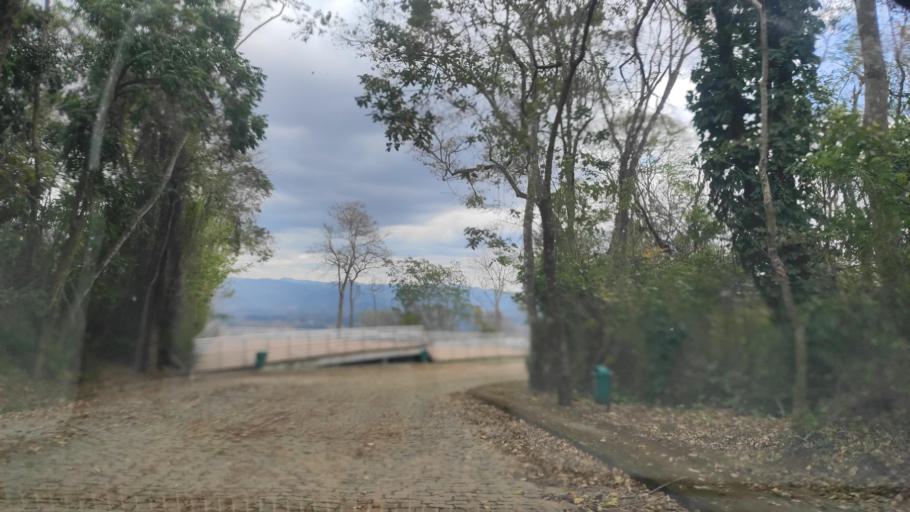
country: BR
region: Espirito Santo
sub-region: Vitoria
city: Vitoria
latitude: -20.3060
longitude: -40.3402
